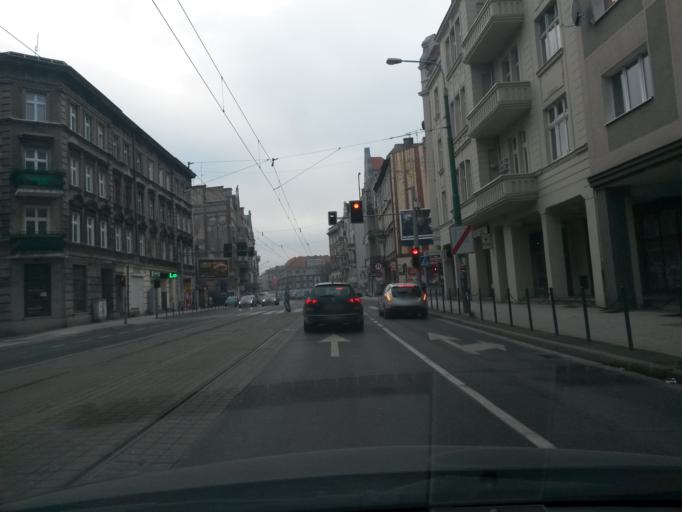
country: PL
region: Greater Poland Voivodeship
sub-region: Poznan
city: Poznan
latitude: 52.3998
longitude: 16.9054
